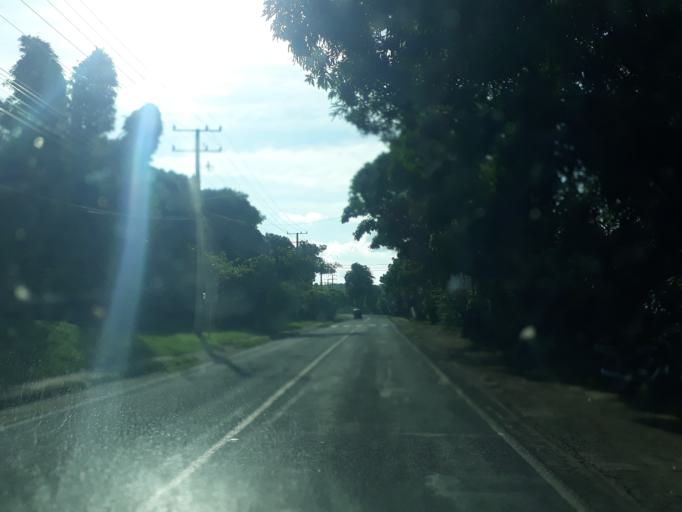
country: NI
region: Masaya
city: Masatepe
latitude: 11.9046
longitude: -86.1628
